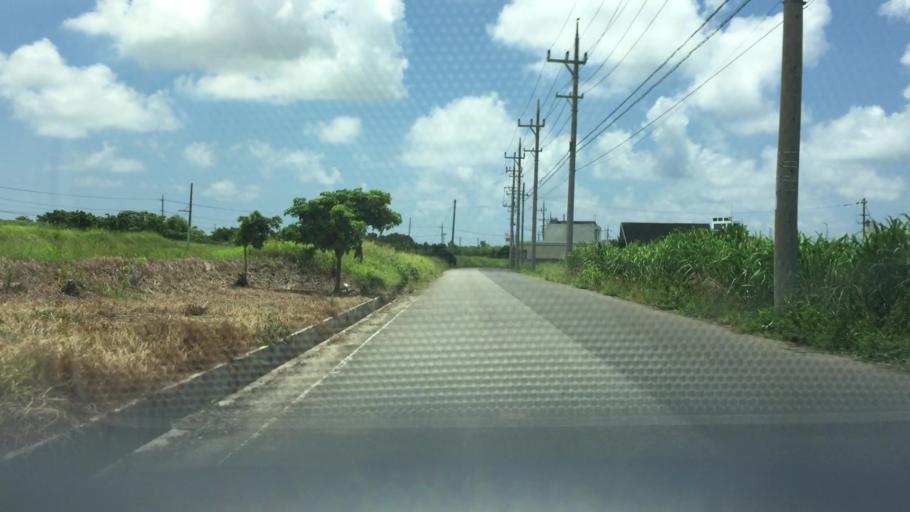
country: JP
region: Okinawa
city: Ishigaki
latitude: 24.3576
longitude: 124.1439
